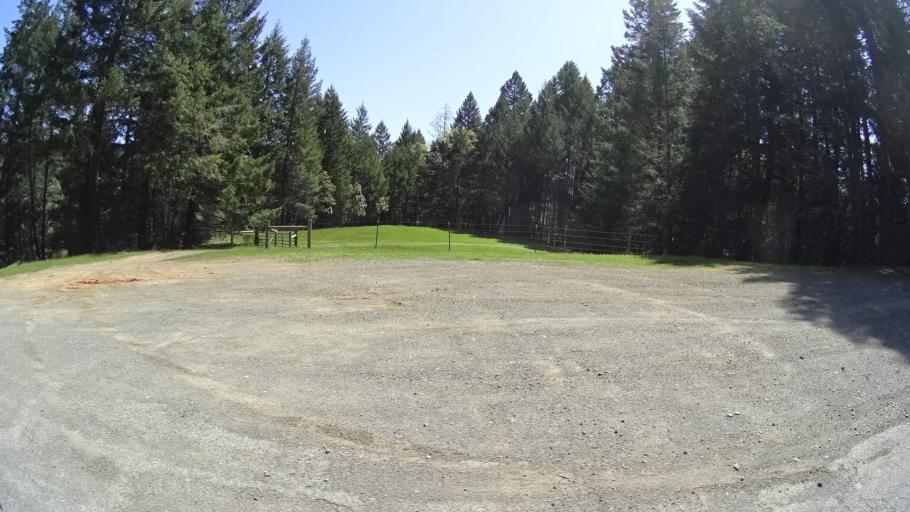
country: US
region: California
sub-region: Humboldt County
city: Redway
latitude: 40.1238
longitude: -123.6399
